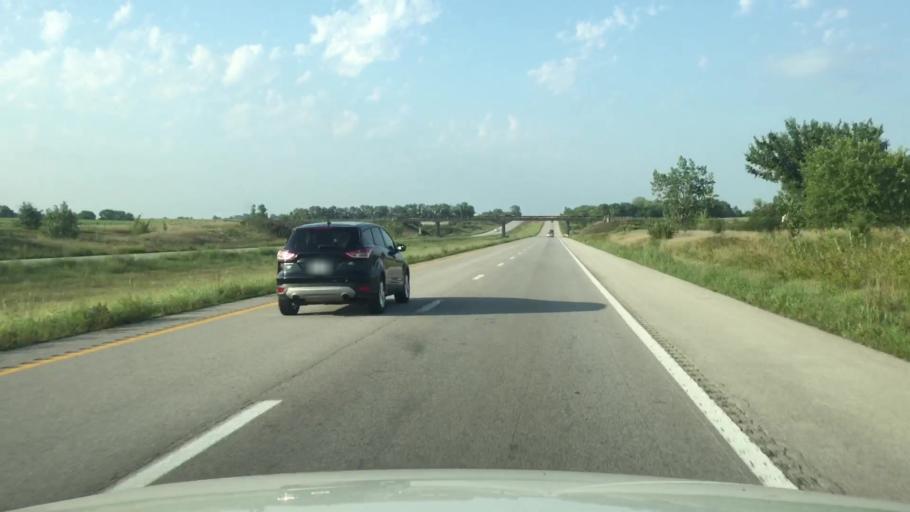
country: US
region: Missouri
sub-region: Clinton County
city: Cameron
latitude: 39.8009
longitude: -94.2000
